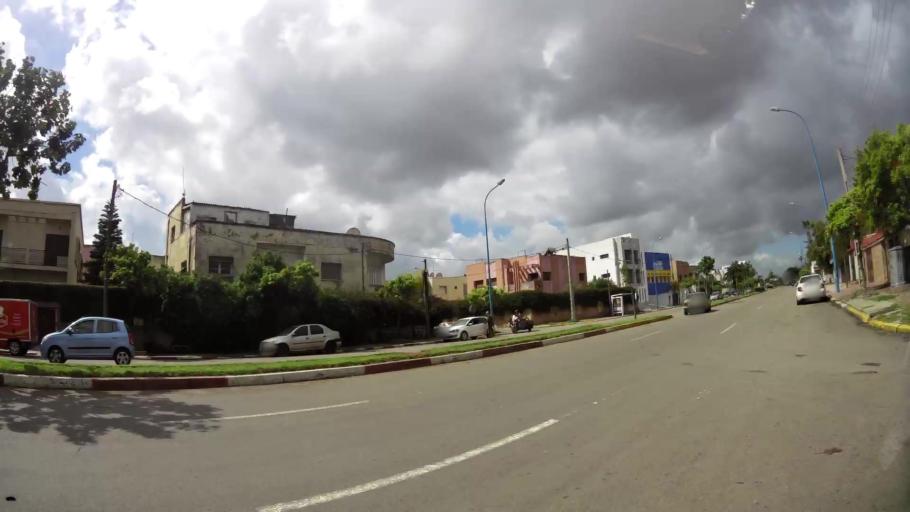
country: MA
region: Grand Casablanca
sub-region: Casablanca
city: Casablanca
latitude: 33.5530
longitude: -7.6065
